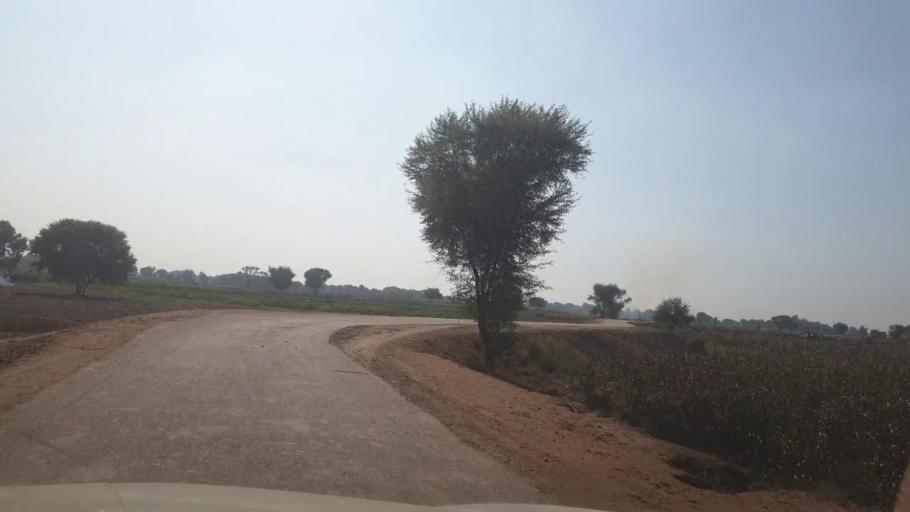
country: PK
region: Sindh
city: Bhan
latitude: 26.5683
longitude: 67.7065
